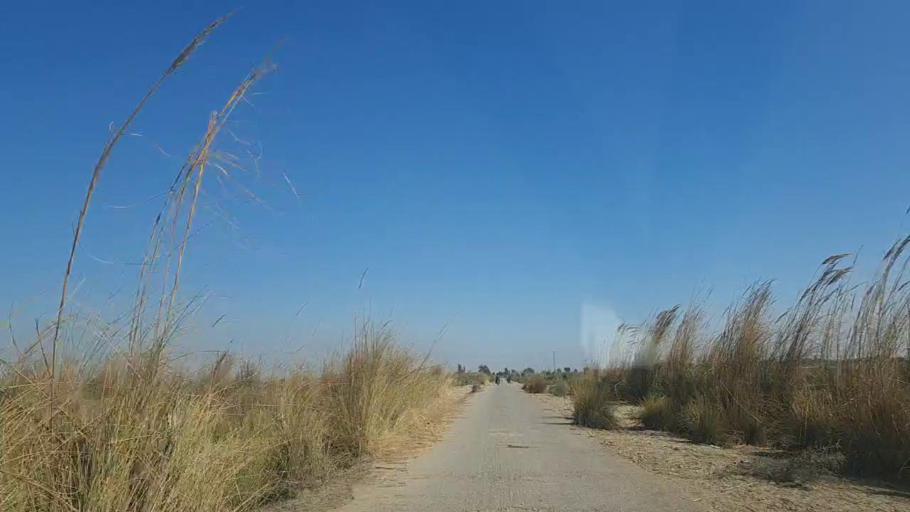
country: PK
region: Sindh
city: Khadro
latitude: 26.2094
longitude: 68.8356
